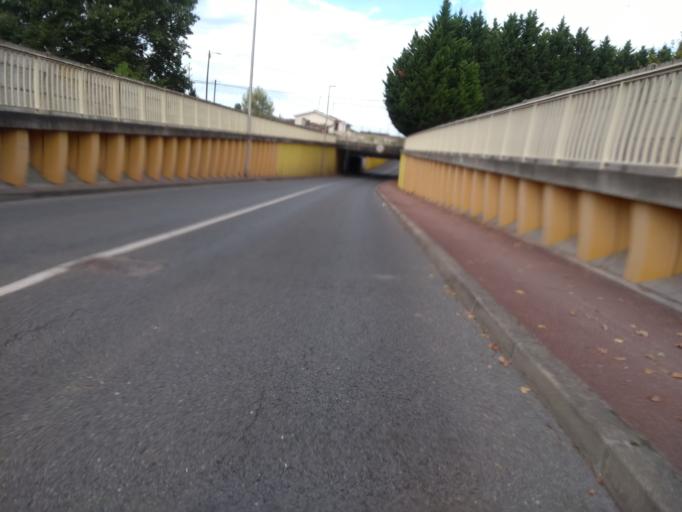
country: FR
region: Aquitaine
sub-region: Departement de la Gironde
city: Cestas
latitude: 44.7825
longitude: -0.6785
